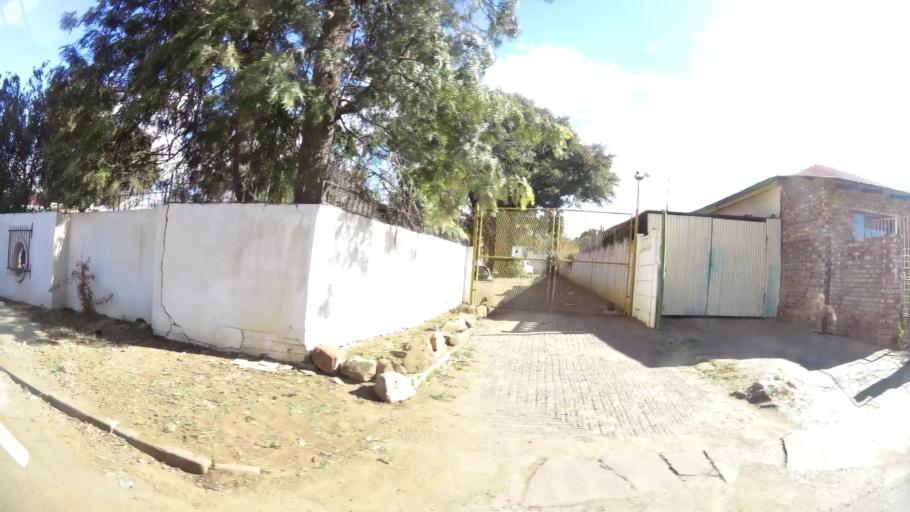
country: ZA
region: North-West
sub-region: Dr Kenneth Kaunda District Municipality
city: Klerksdorp
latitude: -26.8562
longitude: 26.6541
